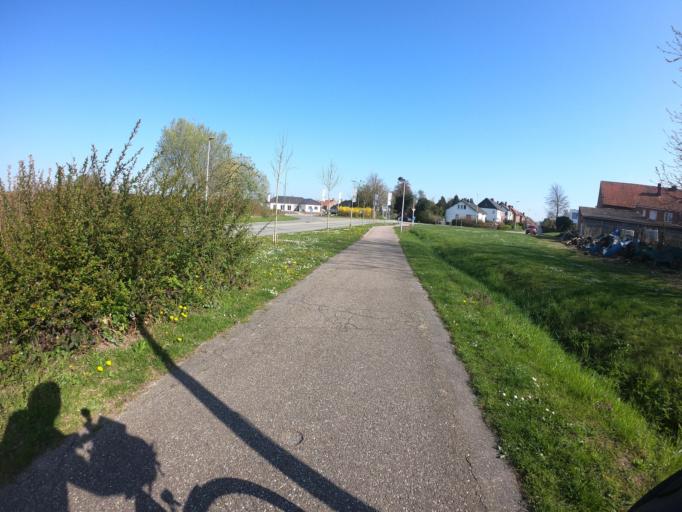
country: BE
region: Flanders
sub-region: Provincie Limburg
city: Sint-Truiden
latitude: 50.8266
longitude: 5.2058
